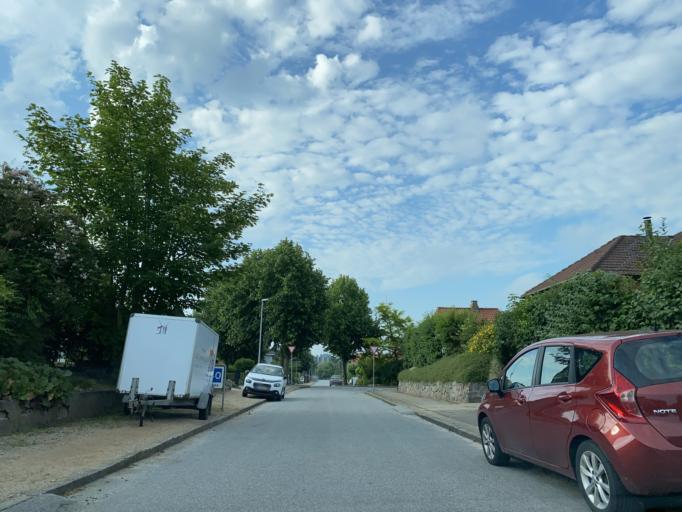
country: DK
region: South Denmark
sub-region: Haderslev Kommune
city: Haderslev
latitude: 55.2420
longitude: 9.4926
